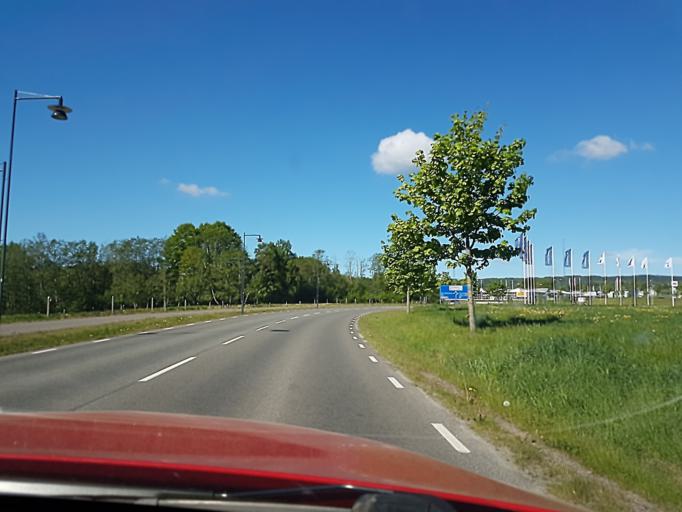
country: SE
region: Vaestra Goetaland
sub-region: Skovde Kommun
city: Skoevde
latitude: 58.4074
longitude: 13.8812
